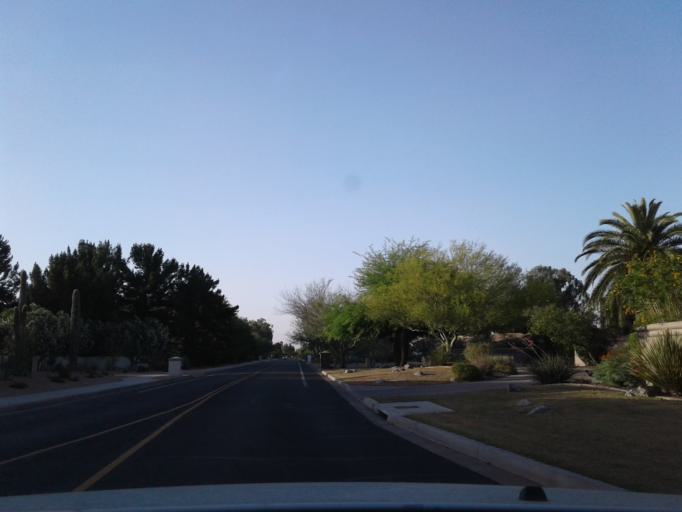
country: US
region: Arizona
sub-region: Maricopa County
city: Paradise Valley
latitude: 33.5684
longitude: -111.9691
